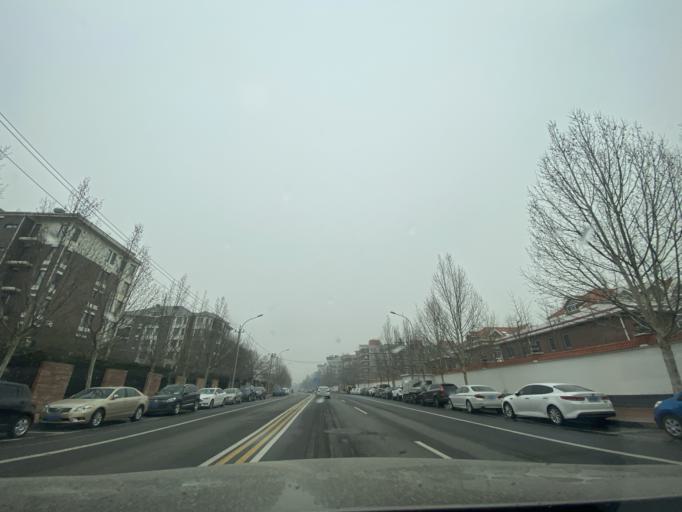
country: CN
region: Beijing
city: Sijiqing
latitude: 39.9596
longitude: 116.2421
